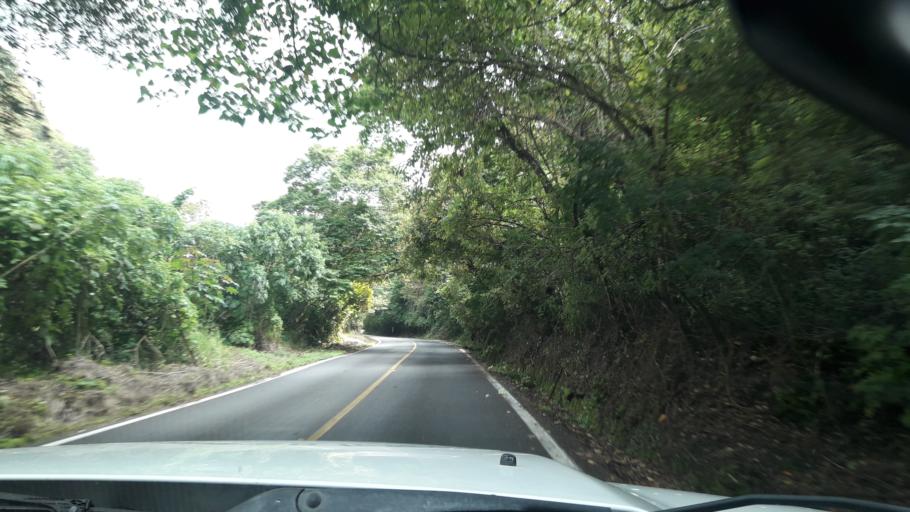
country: MX
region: Colima
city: Suchitlan
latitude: 19.4396
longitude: -103.7141
